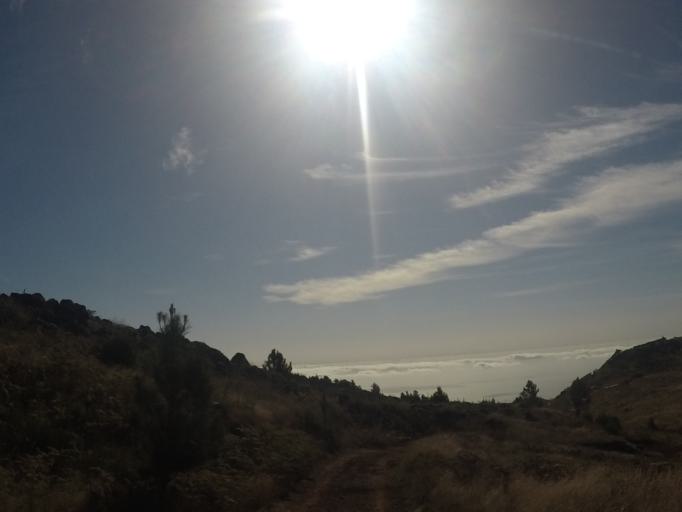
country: PT
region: Madeira
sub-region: Funchal
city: Nossa Senhora do Monte
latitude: 32.7033
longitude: -16.8989
